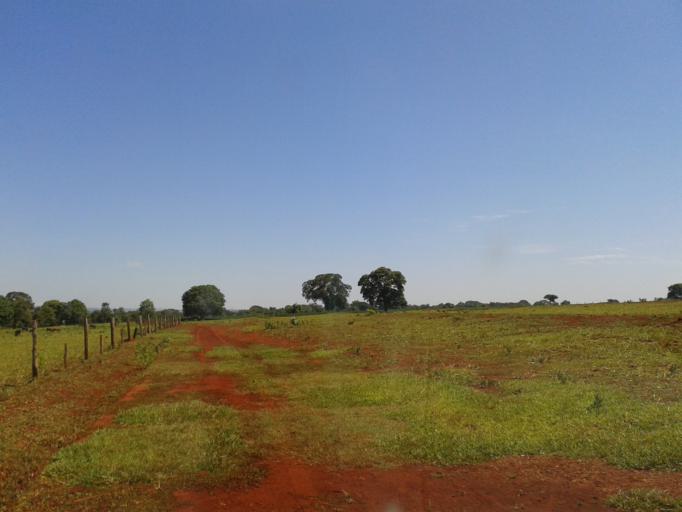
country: BR
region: Minas Gerais
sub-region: Centralina
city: Centralina
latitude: -18.6377
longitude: -49.2947
